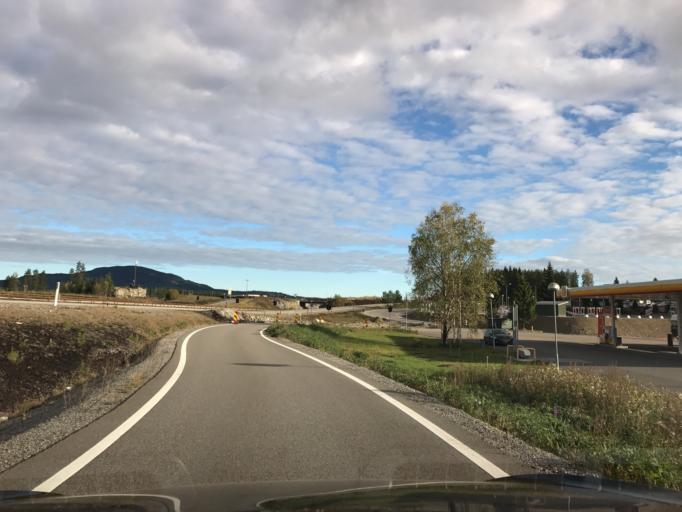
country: NO
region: Akershus
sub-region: Eidsvoll
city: Raholt
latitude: 60.3114
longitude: 11.1431
